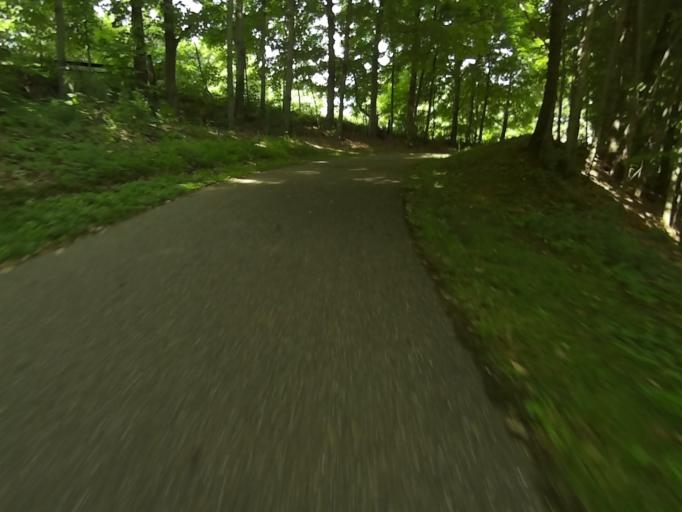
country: US
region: Ohio
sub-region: Summit County
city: Stow
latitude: 41.1908
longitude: -81.4015
